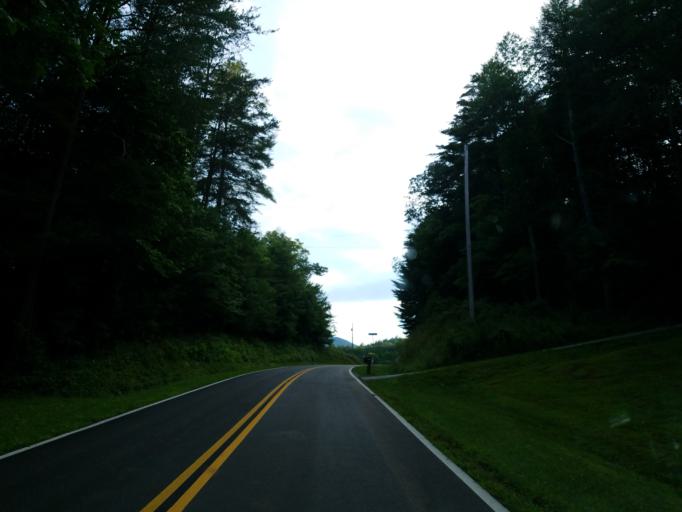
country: US
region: Georgia
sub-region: Union County
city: Blairsville
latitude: 34.7385
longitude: -84.0598
